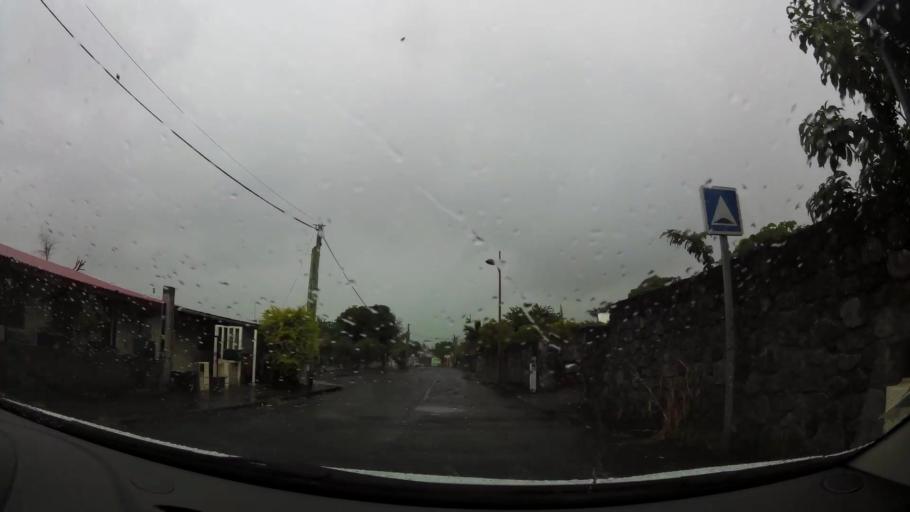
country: RE
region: Reunion
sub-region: Reunion
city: Saint-Andre
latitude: -20.9775
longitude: 55.6581
